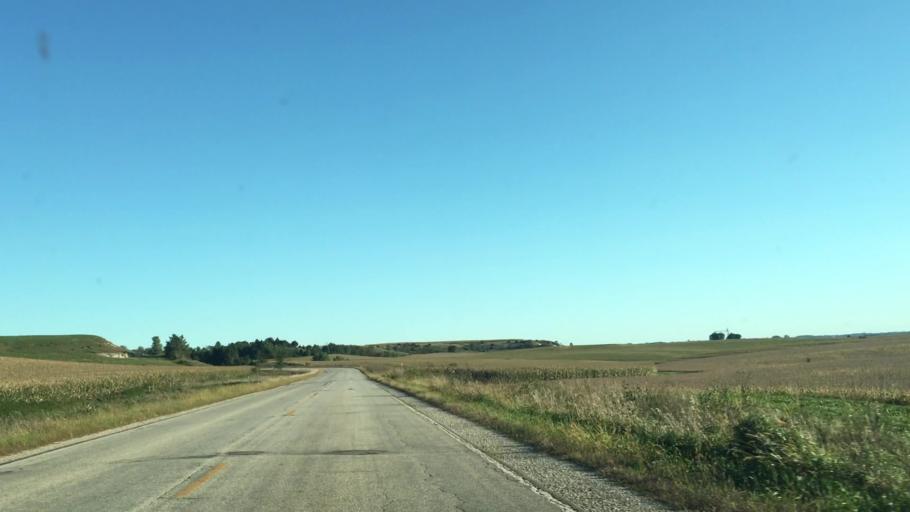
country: US
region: Minnesota
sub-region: Fillmore County
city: Chatfield
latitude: 43.8503
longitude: -92.1073
